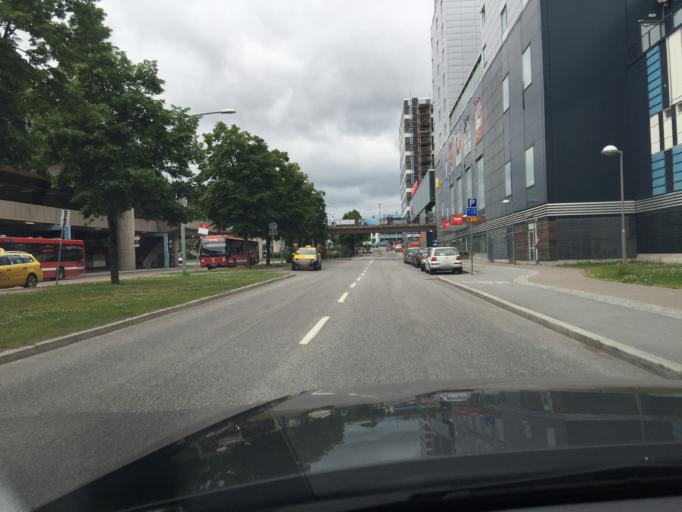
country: SE
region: Stockholm
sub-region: Stockholms Kommun
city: Kista
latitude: 59.4031
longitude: 17.9433
